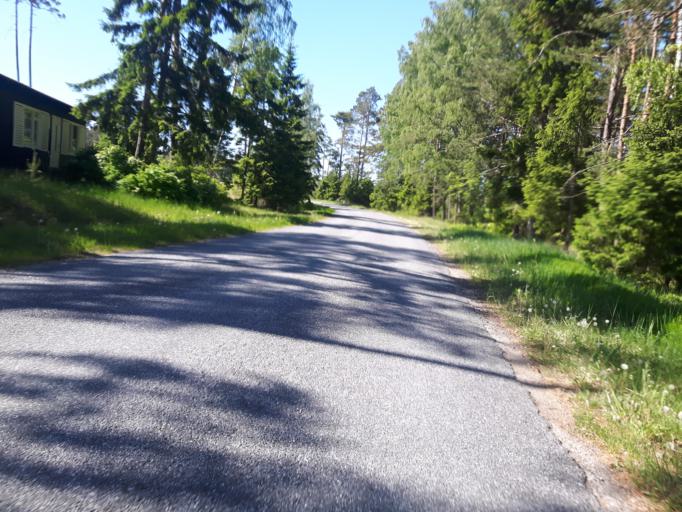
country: EE
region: Laeaene-Virumaa
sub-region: Haljala vald
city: Haljala
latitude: 59.5705
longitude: 26.2907
